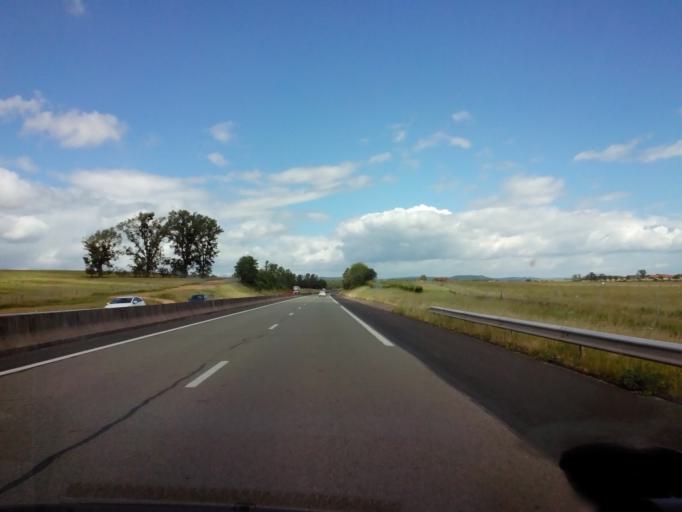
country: FR
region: Lorraine
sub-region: Departement des Vosges
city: Lamarche
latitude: 48.1197
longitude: 5.6628
